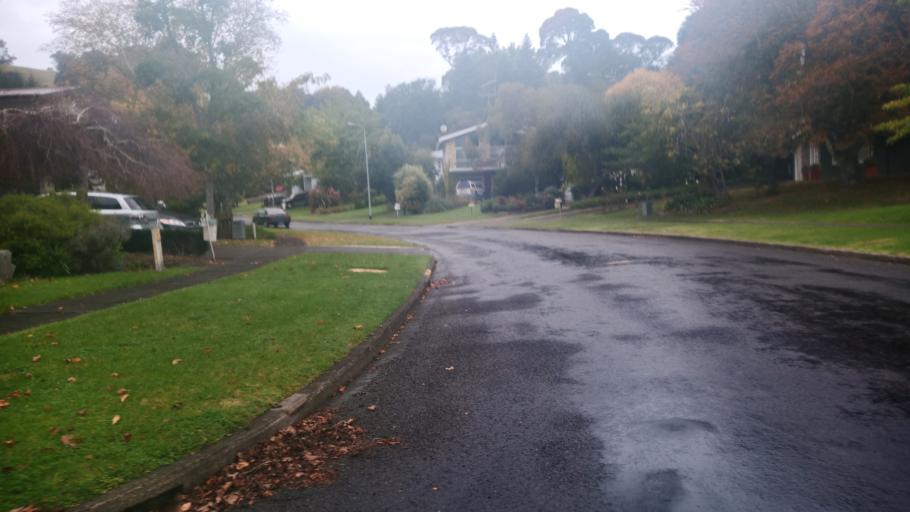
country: NZ
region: Gisborne
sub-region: Gisborne District
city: Gisborne
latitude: -38.6579
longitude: 178.0392
